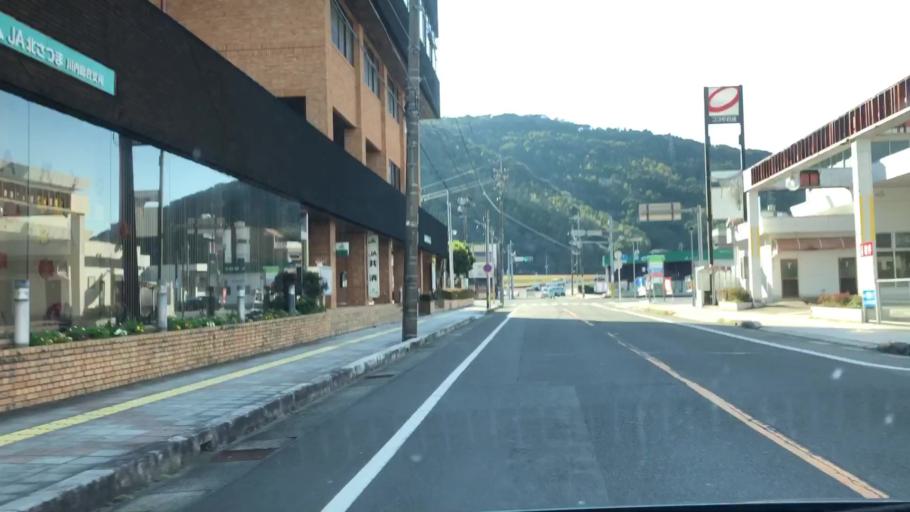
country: JP
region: Kagoshima
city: Satsumasendai
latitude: 31.8151
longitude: 130.3014
